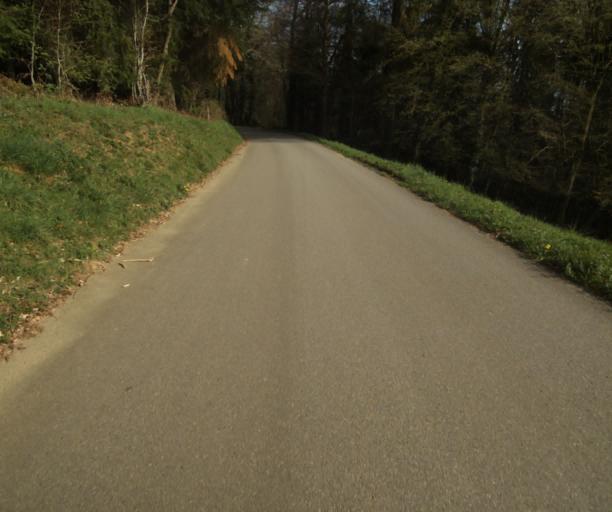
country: FR
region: Limousin
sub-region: Departement de la Correze
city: Naves
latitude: 45.3243
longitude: 1.7265
